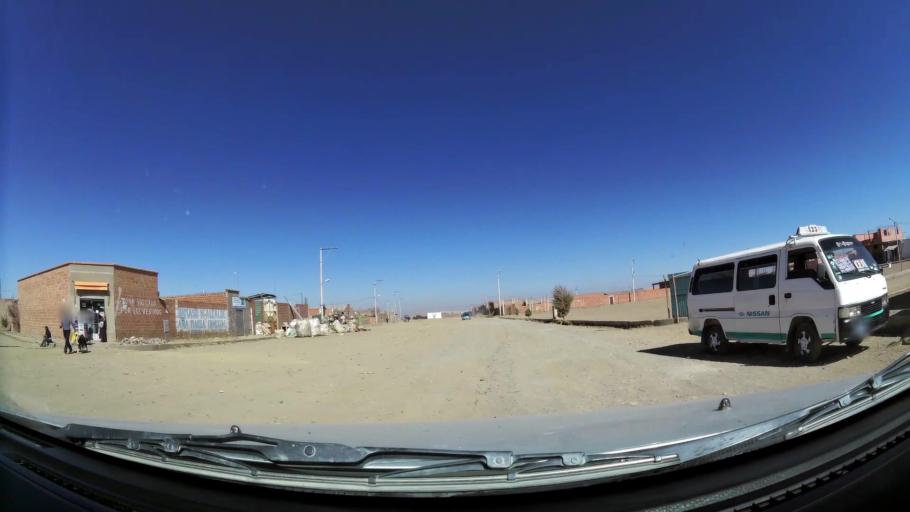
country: BO
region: La Paz
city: La Paz
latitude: -16.6248
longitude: -68.1922
